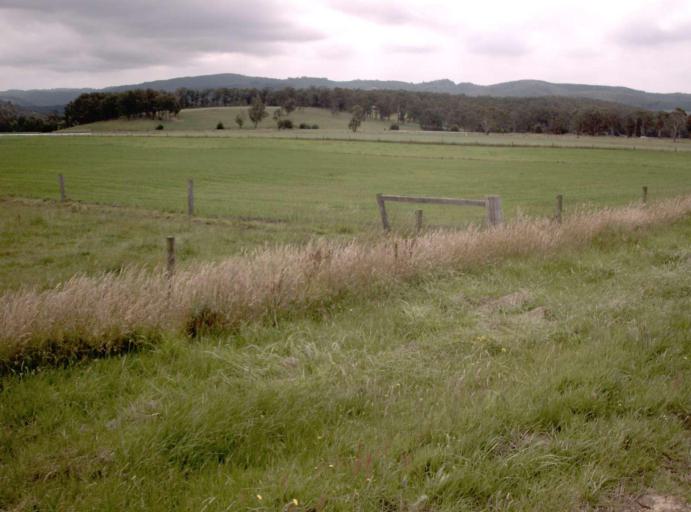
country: AU
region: Victoria
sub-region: Latrobe
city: Traralgon
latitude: -38.4936
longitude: 146.6793
